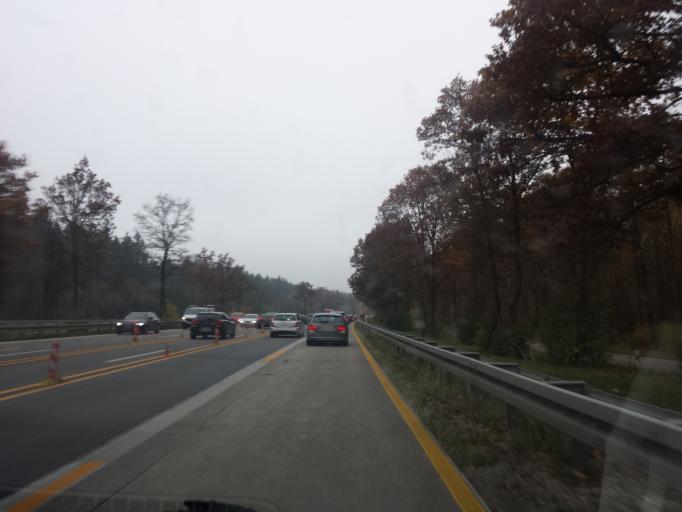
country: DE
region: Bavaria
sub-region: Upper Bavaria
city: Baierbrunn
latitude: 48.0480
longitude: 11.4494
